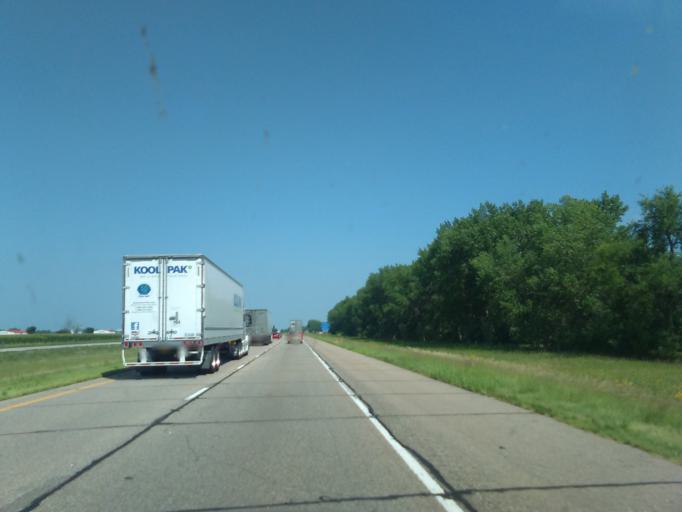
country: US
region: Nebraska
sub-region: Buffalo County
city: Kearney
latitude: 40.6717
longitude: -99.1683
